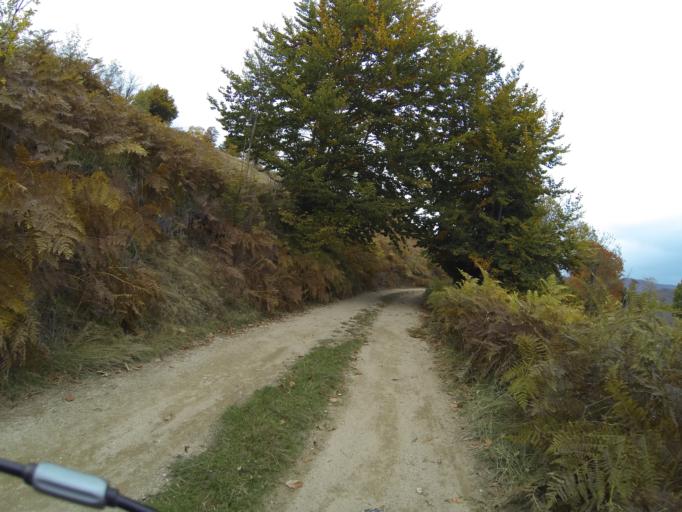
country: RO
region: Gorj
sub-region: Comuna Pades
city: Closani
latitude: 45.1055
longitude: 22.8457
